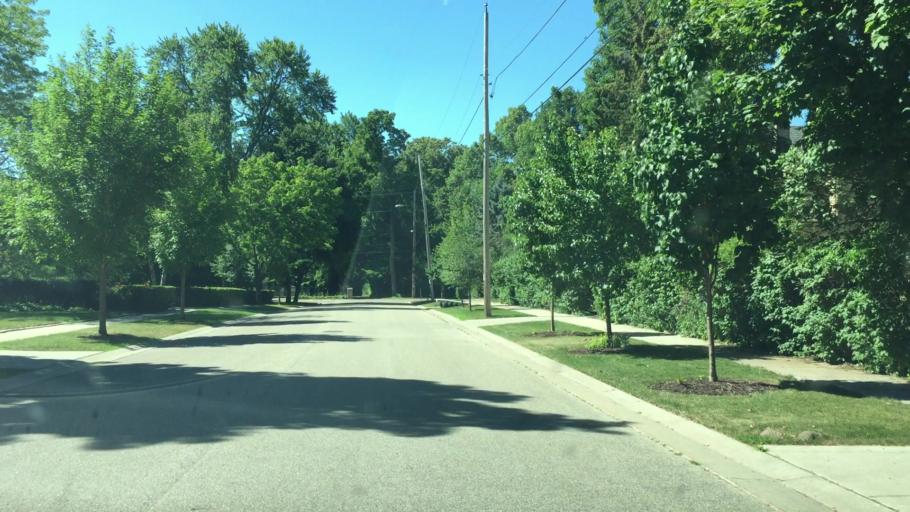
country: US
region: Wisconsin
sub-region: Winnebago County
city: Menasha
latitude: 44.1912
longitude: -88.4446
